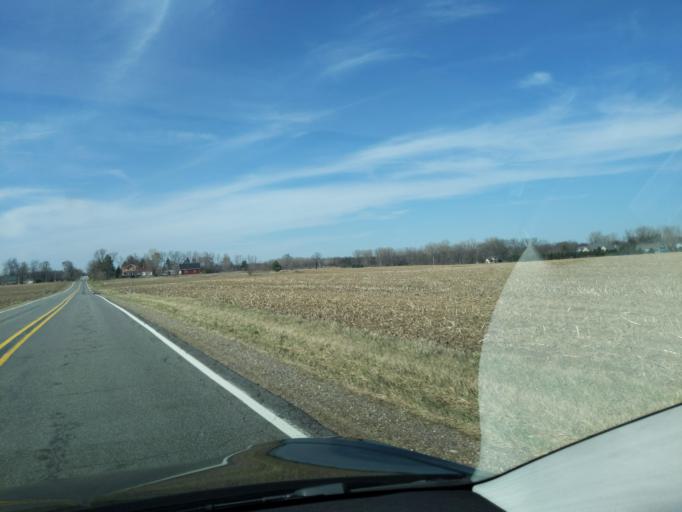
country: US
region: Michigan
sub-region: Ingham County
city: Williamston
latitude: 42.6544
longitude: -84.3112
